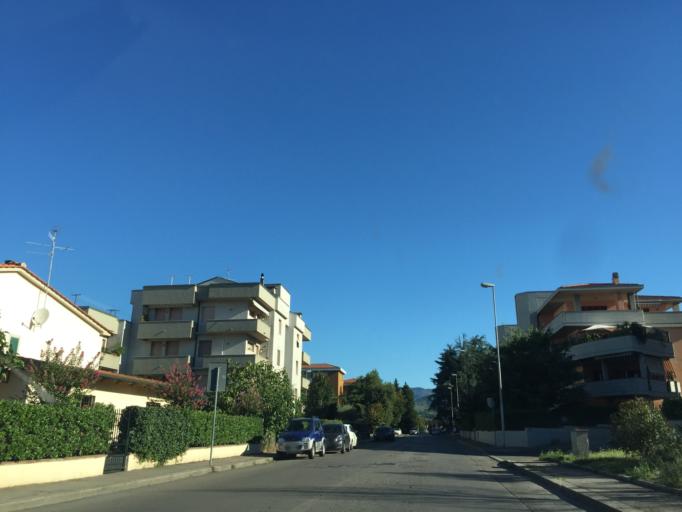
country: IT
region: Tuscany
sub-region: Provincia di Pistoia
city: Pistoia
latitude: 43.9357
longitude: 10.8975
